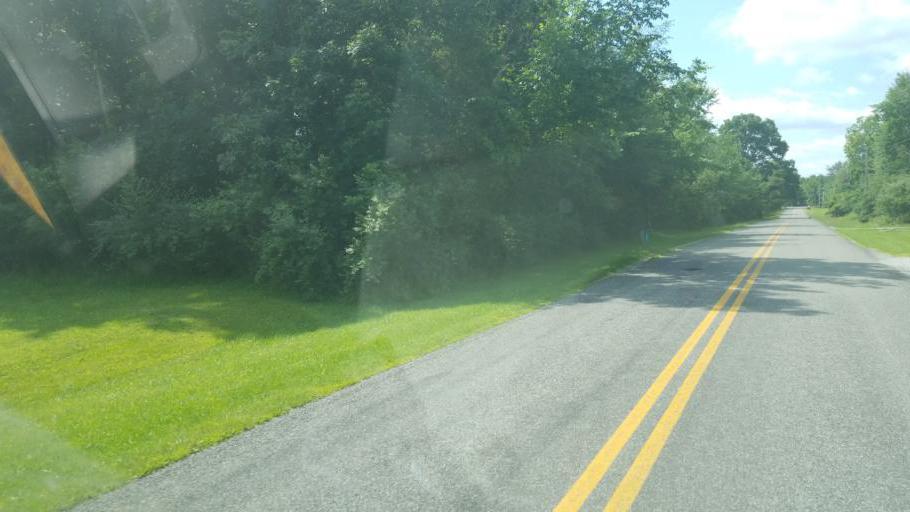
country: US
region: Ohio
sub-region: Delaware County
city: Sunbury
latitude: 40.2931
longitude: -82.9451
